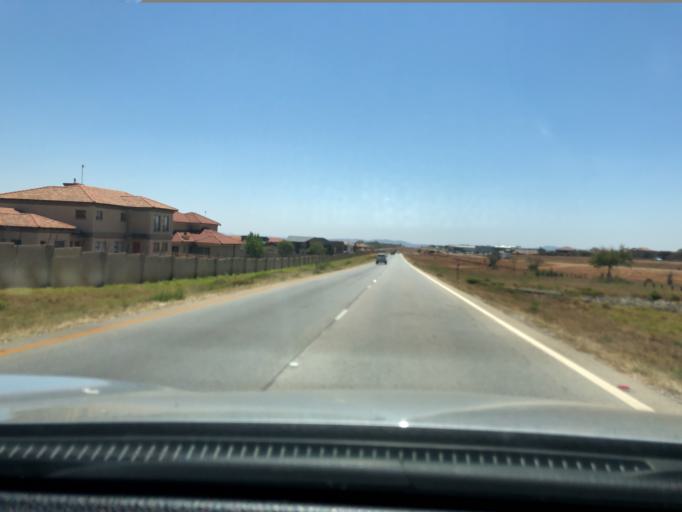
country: ZA
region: Limpopo
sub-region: Capricorn District Municipality
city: Polokwane
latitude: -23.8877
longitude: 29.5079
